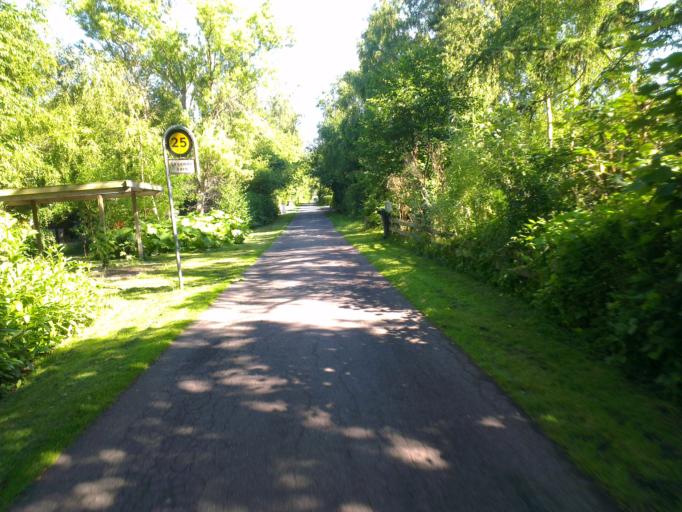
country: DK
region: Capital Region
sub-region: Frederikssund Kommune
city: Jaegerspris
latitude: 55.9133
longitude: 11.9202
